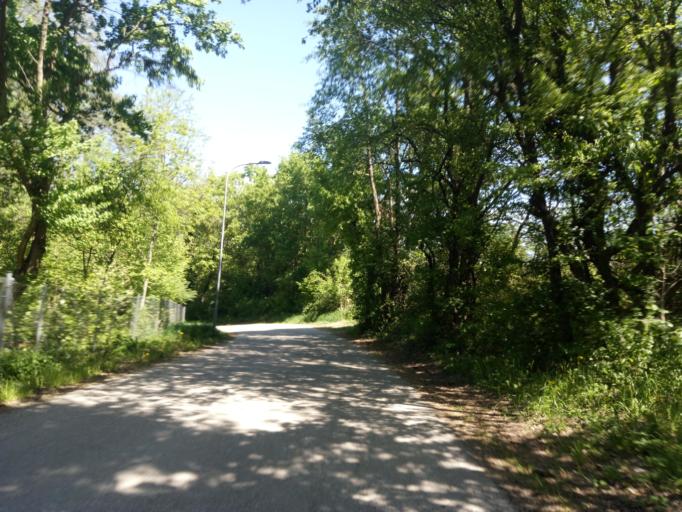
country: AT
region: Lower Austria
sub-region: Politischer Bezirk Modling
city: Kaltenleutgeben
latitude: 48.1270
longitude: 16.1880
